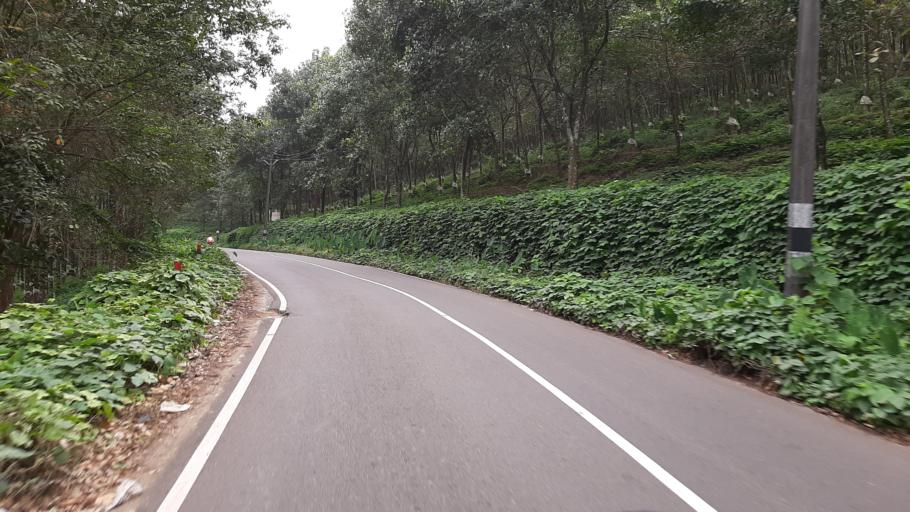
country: IN
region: Kerala
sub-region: Pattanamtitta
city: Pathanamthitta
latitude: 9.4632
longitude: 76.8696
